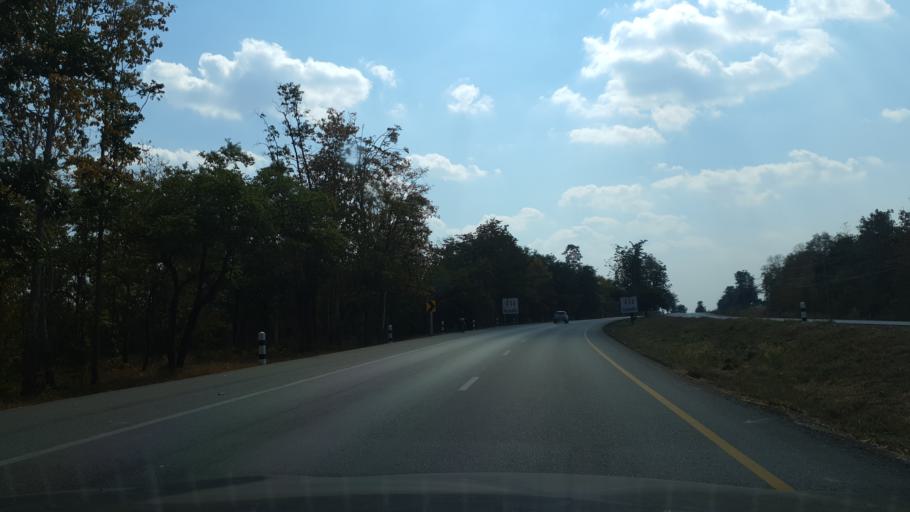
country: TH
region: Lampang
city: Mae Phrik
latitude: 17.3326
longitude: 99.1542
